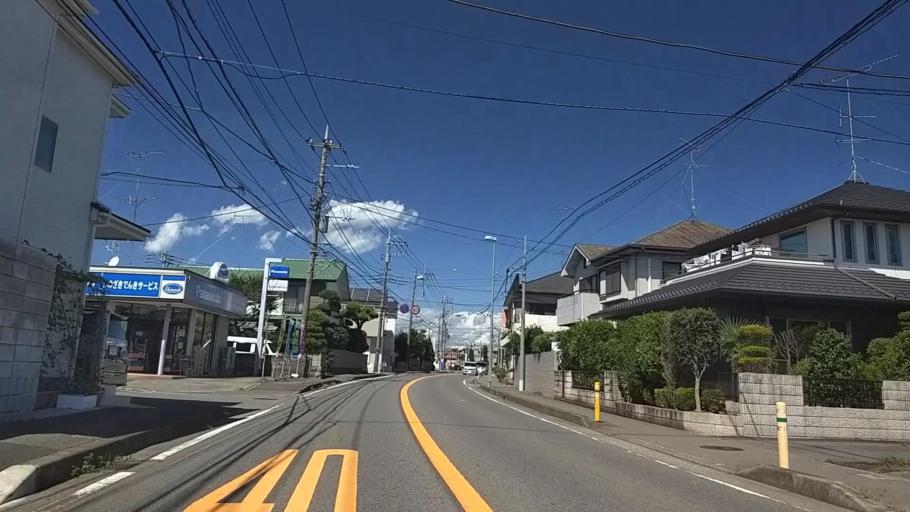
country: JP
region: Kanagawa
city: Zama
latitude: 35.5530
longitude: 139.3329
